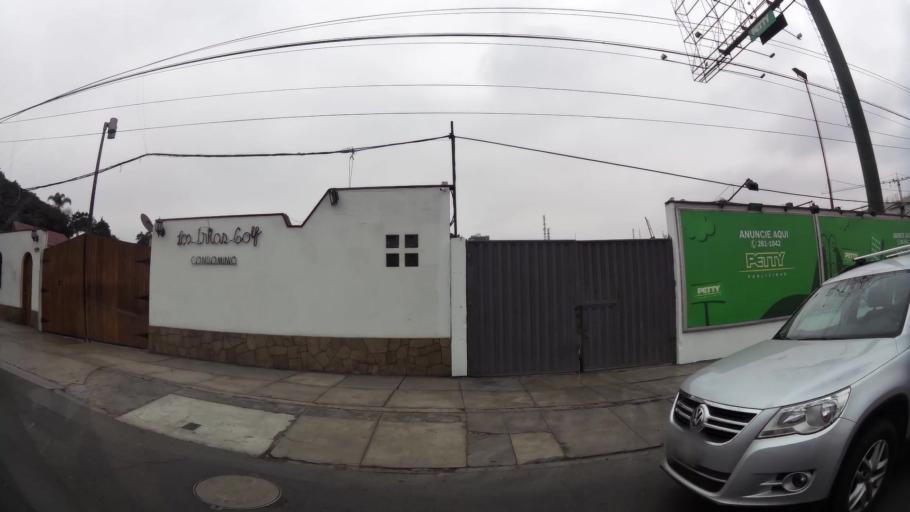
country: PE
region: Lima
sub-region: Lima
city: La Molina
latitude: -12.0791
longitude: -76.9655
